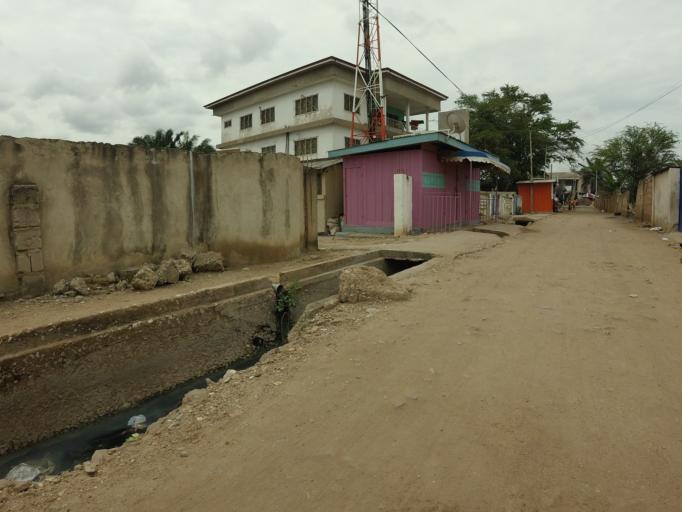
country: GH
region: Greater Accra
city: Accra
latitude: 5.5945
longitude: -0.2175
